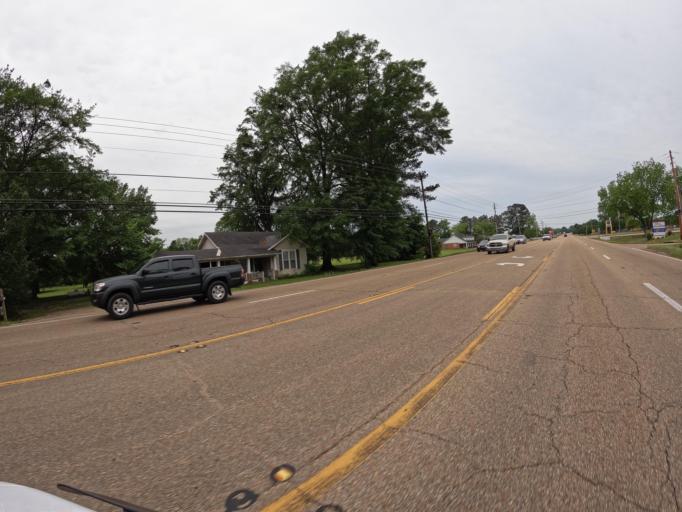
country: US
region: Mississippi
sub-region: Lee County
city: Tupelo
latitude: 34.2943
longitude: -88.7616
